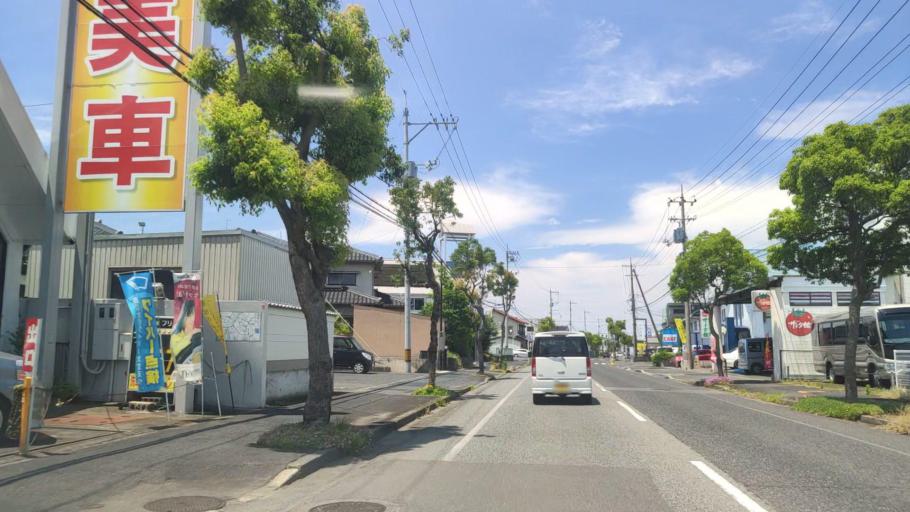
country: JP
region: Tottori
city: Tottori
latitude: 35.4783
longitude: 134.2359
